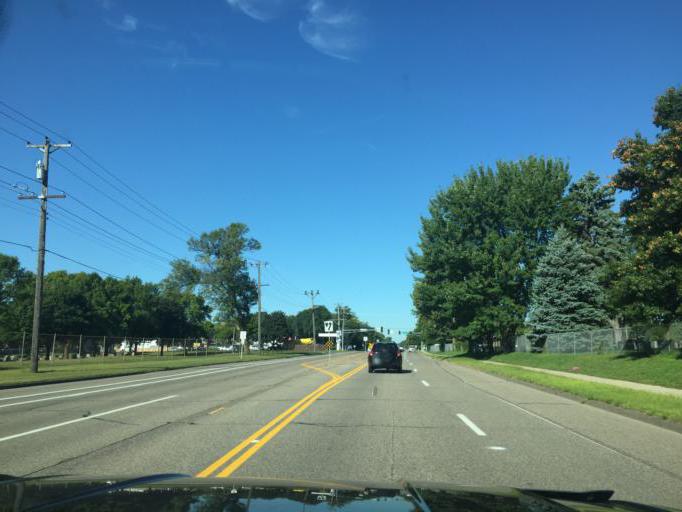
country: US
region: Minnesota
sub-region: Ramsey County
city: Roseville
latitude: 44.9918
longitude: -93.1238
